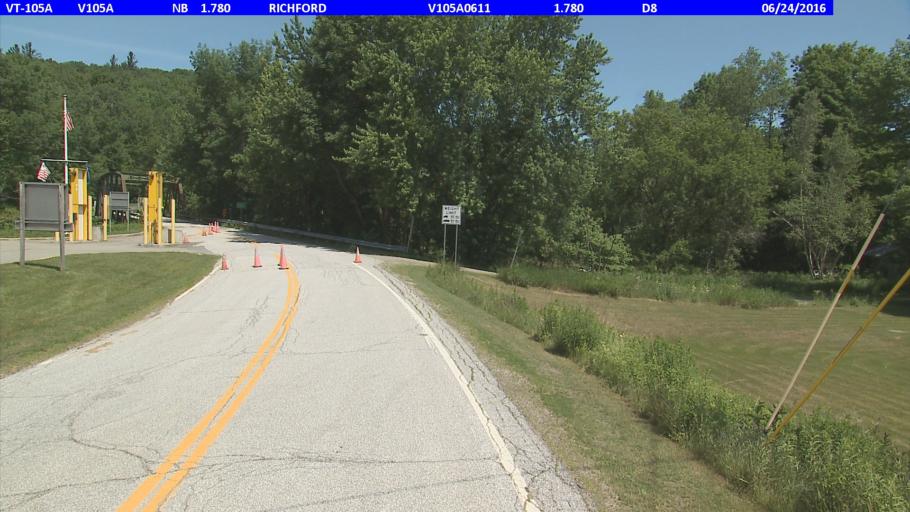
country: US
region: Vermont
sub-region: Franklin County
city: Richford
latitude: 45.0109
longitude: -72.5874
